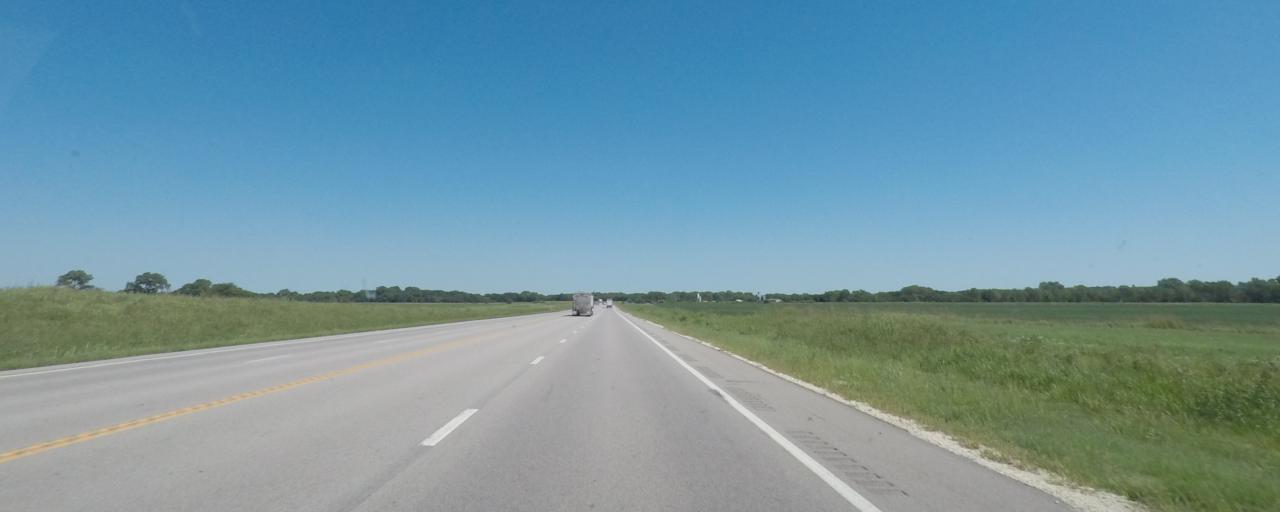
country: US
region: Kansas
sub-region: Chase County
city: Cottonwood Falls
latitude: 38.4052
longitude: -96.4063
